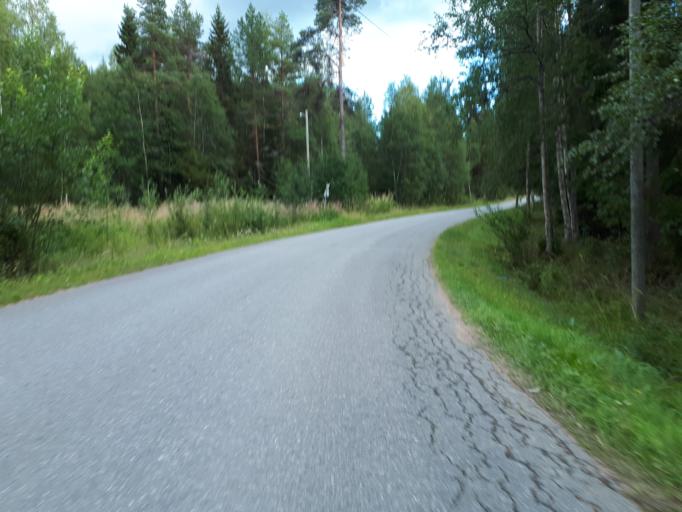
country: FI
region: Northern Ostrobothnia
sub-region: Oulunkaari
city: Ii
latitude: 65.3312
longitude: 25.3954
